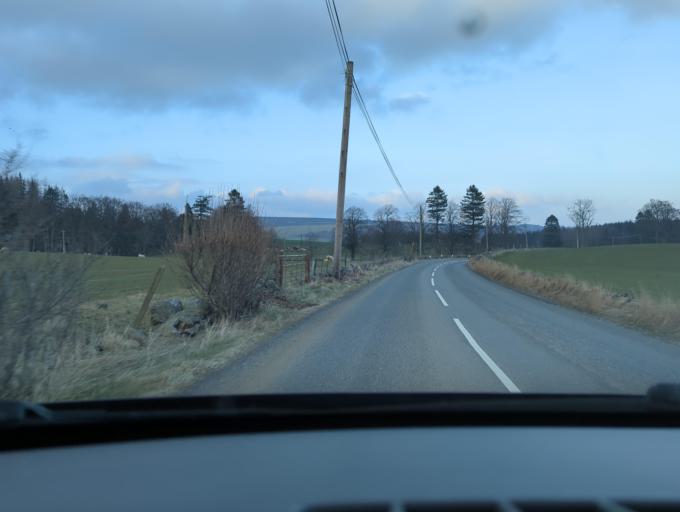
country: GB
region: Scotland
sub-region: Perth and Kinross
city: Aberfeldy
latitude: 56.5304
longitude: -3.7195
